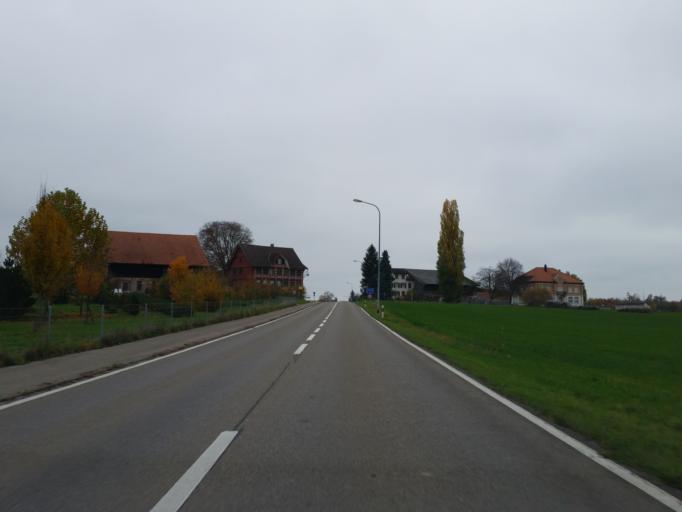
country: CH
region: Thurgau
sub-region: Arbon District
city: Amriswil
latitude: 47.5615
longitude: 9.3114
